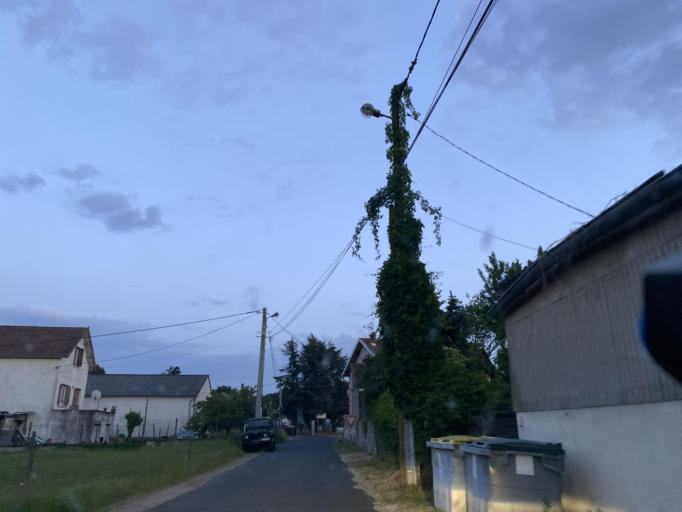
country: FR
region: Auvergne
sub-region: Departement du Puy-de-Dome
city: Courpiere
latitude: 45.7489
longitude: 3.5459
